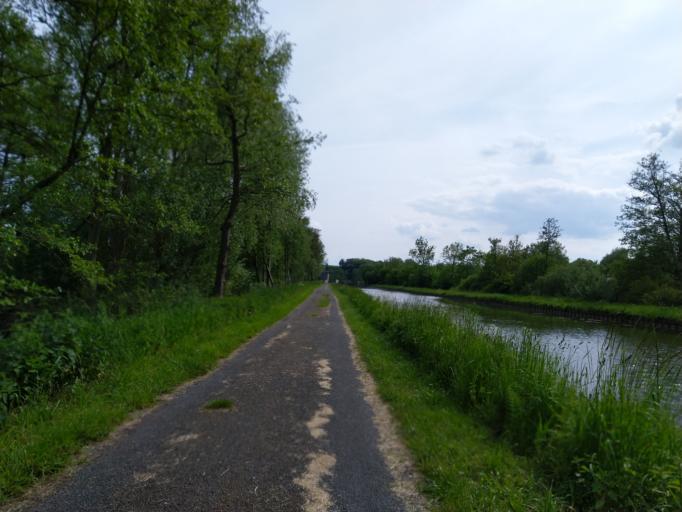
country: FR
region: Picardie
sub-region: Departement de l'Aisne
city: Etreux
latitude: 49.9634
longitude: 3.6182
